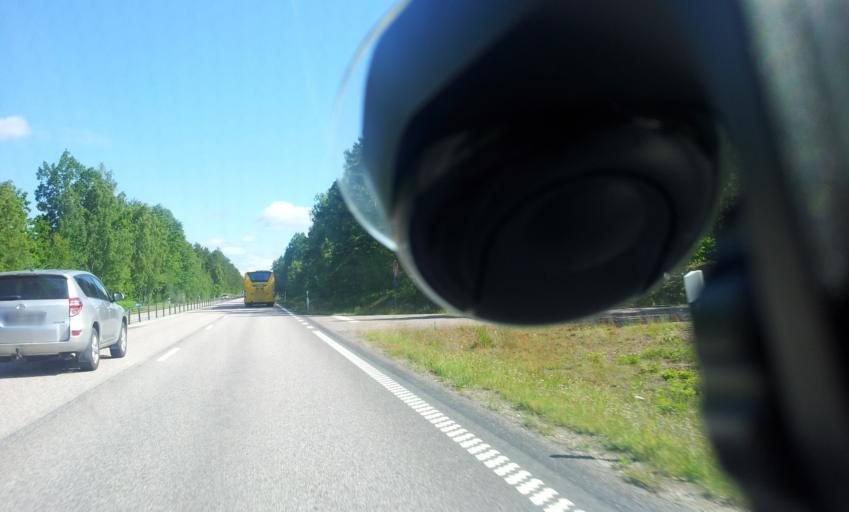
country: SE
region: Kalmar
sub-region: Monsteras Kommun
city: Timmernabben
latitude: 56.9938
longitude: 16.4126
